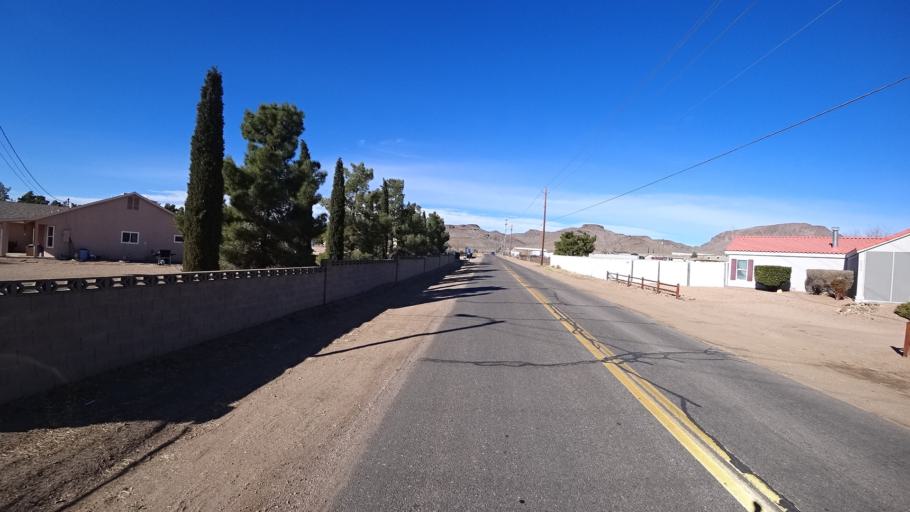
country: US
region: Arizona
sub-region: Mohave County
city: New Kingman-Butler
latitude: 35.2466
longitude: -114.0353
